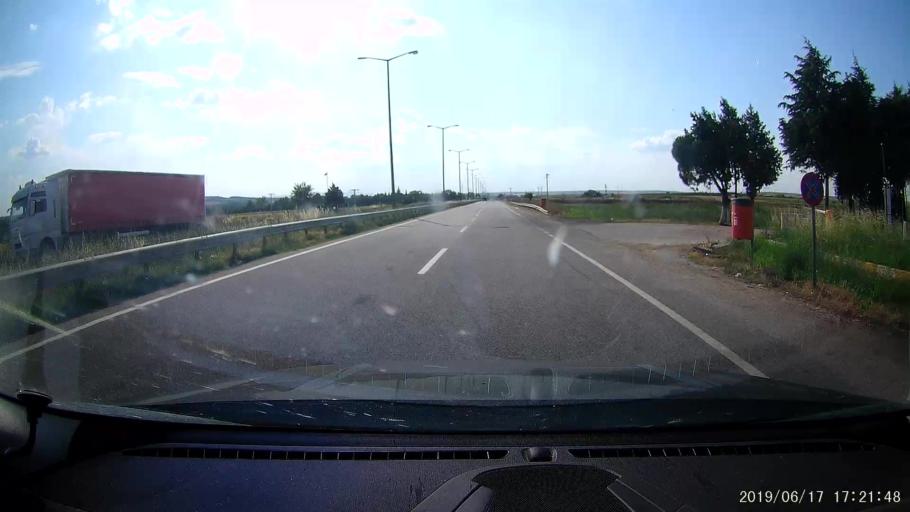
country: GR
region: East Macedonia and Thrace
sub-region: Nomos Evrou
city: Rizia
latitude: 41.7081
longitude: 26.3871
